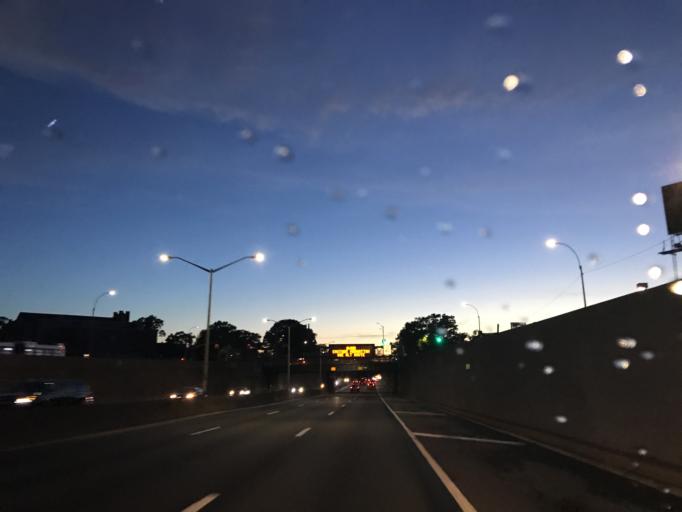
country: US
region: New York
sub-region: Queens County
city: Long Island City
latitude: 40.7673
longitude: -73.8998
